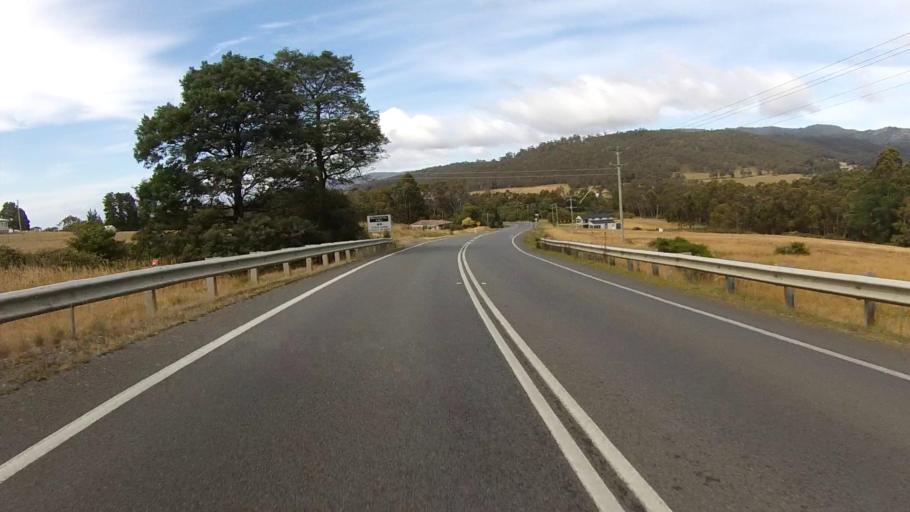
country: AU
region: Tasmania
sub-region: Kingborough
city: Kettering
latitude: -43.1157
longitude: 147.2450
